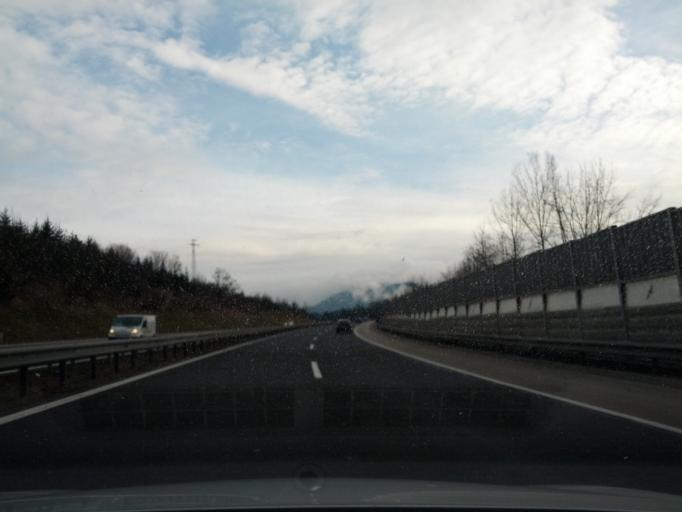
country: SI
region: Naklo
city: Naklo
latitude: 46.2881
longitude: 14.2883
